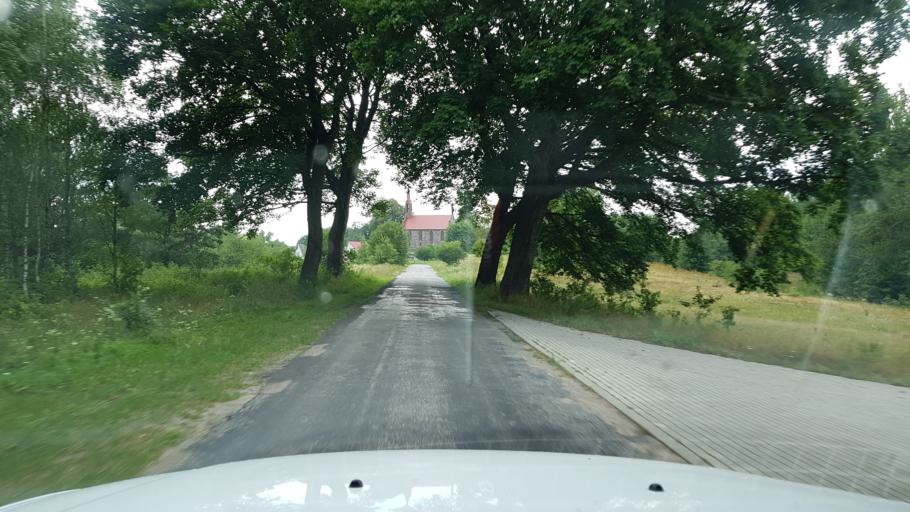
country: PL
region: West Pomeranian Voivodeship
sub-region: Powiat koszalinski
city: Bobolice
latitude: 53.9253
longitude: 16.6575
